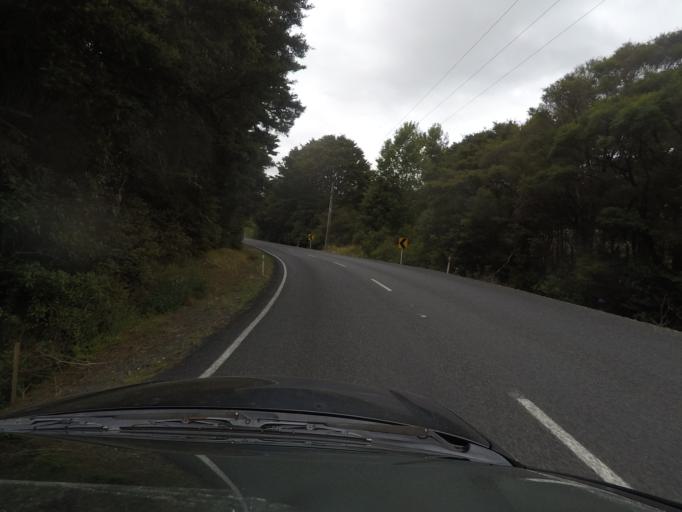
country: NZ
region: Auckland
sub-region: Auckland
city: Wellsford
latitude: -36.2793
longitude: 174.5848
